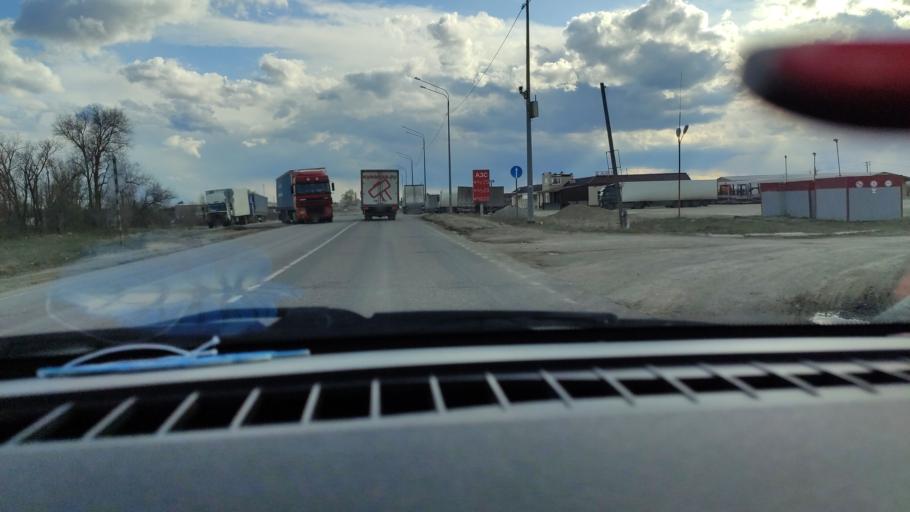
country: RU
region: Saratov
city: Sinodskoye
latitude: 51.9954
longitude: 46.6729
